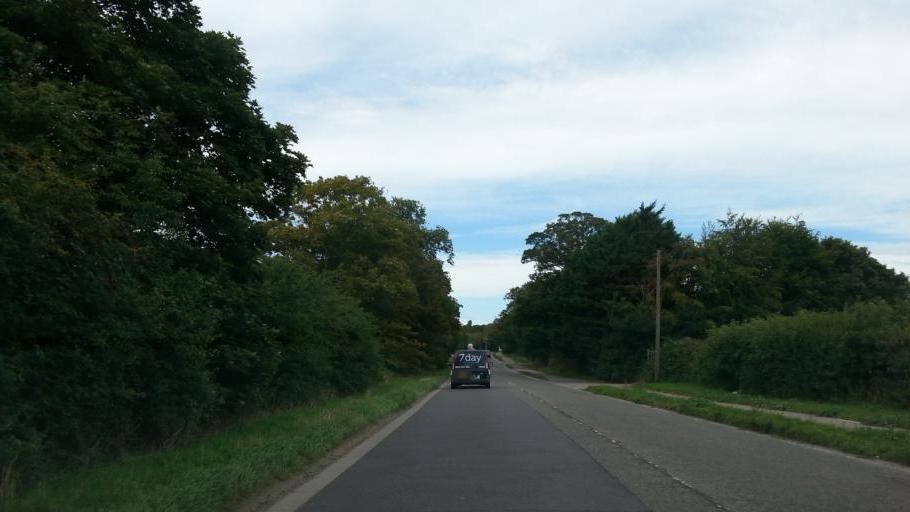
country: GB
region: England
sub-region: Cambridgeshire
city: Sawston
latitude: 52.1515
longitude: 0.1892
